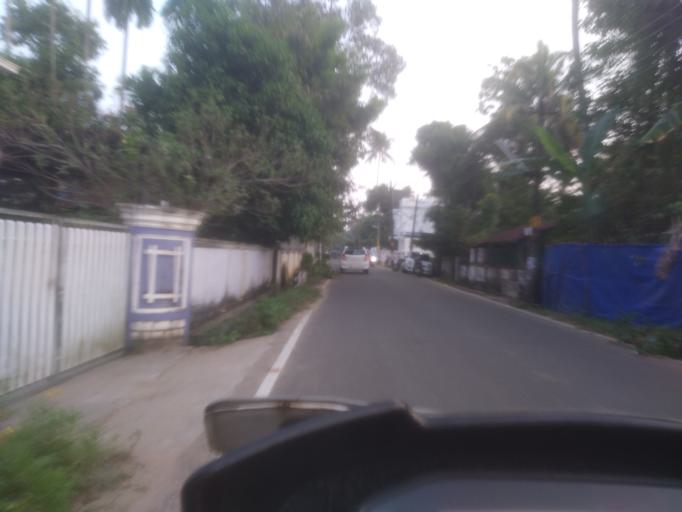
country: IN
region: Kerala
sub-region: Ernakulam
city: Cochin
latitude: 10.0072
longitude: 76.2194
